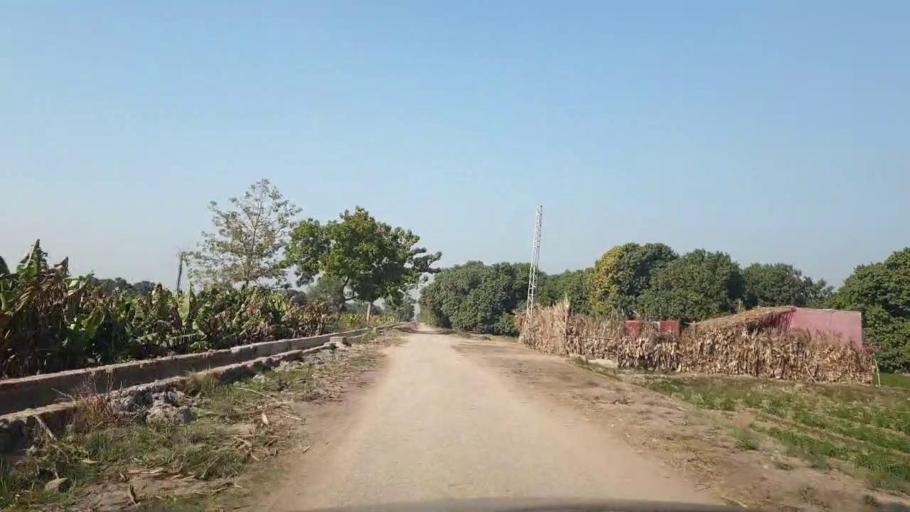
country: PK
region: Sindh
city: Tando Allahyar
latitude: 25.5152
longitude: 68.7017
